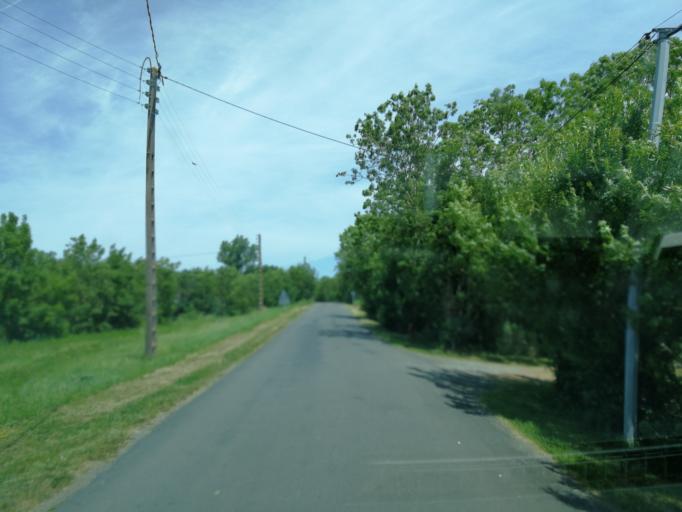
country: FR
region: Pays de la Loire
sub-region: Departement de la Vendee
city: Le Langon
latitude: 46.3968
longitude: -0.9324
